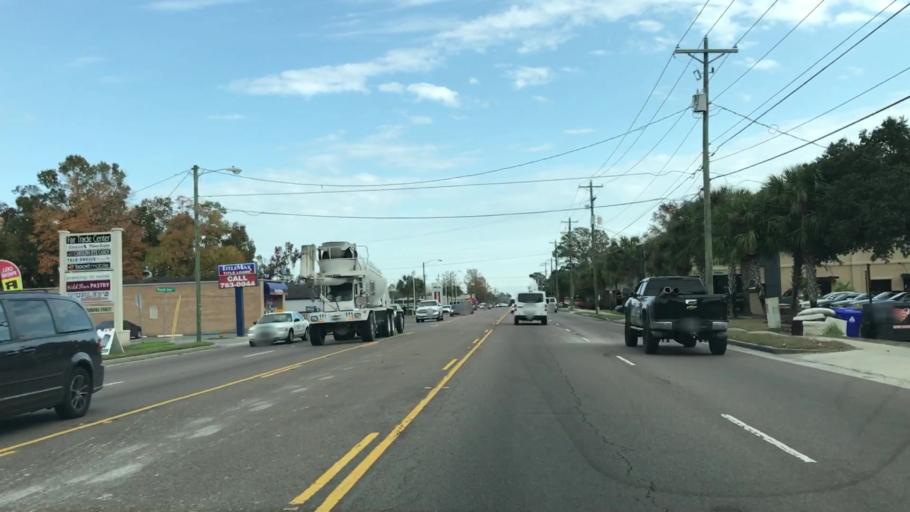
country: US
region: South Carolina
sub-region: Charleston County
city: North Charleston
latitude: 32.7879
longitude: -80.0195
